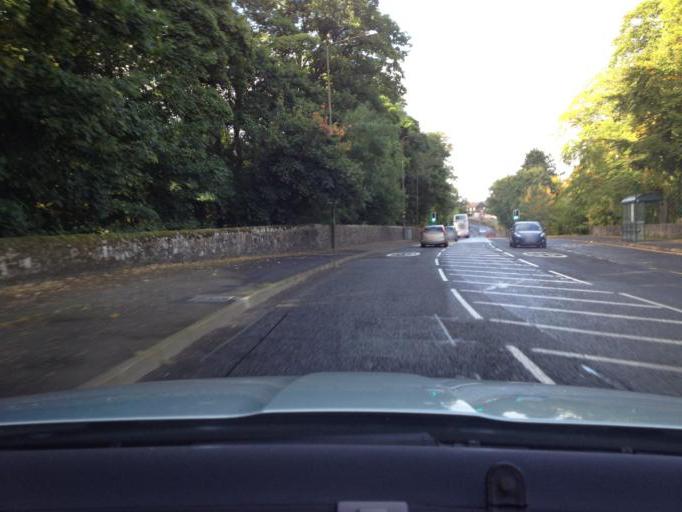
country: GB
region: Scotland
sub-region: West Lothian
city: West Calder
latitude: 55.8638
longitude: -3.5409
